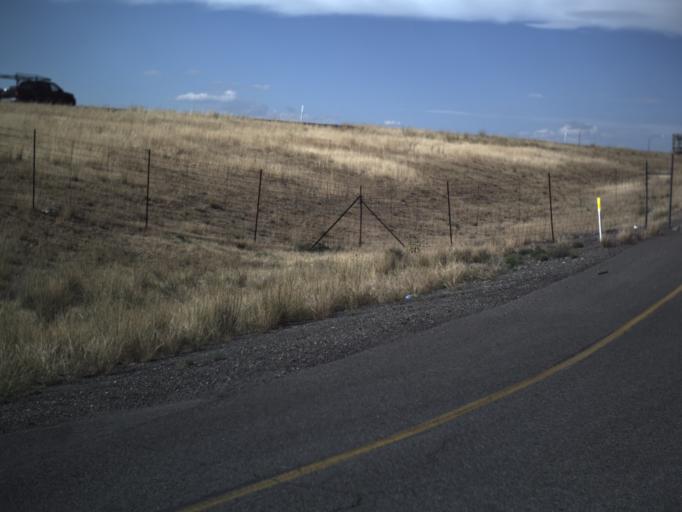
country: US
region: Utah
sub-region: Juab County
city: Mona
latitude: 39.8215
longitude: -111.8327
